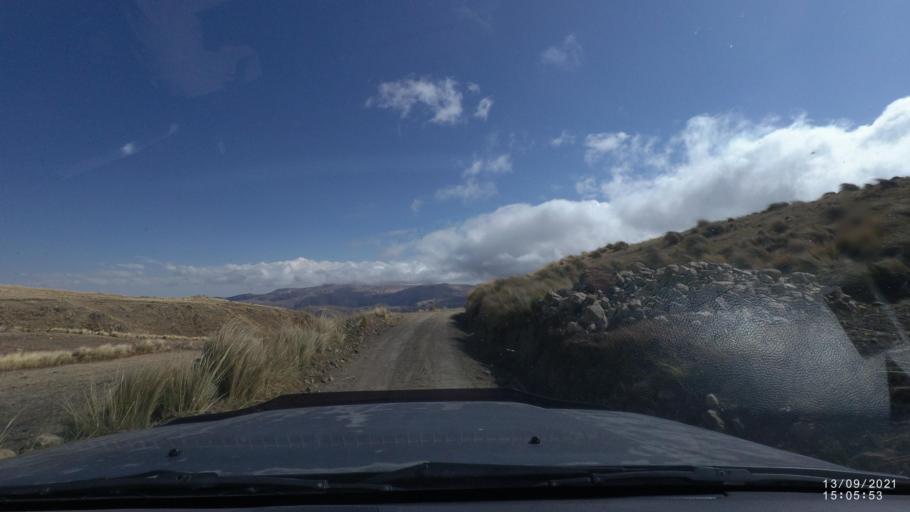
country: BO
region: Cochabamba
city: Colomi
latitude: -17.3461
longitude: -65.7931
